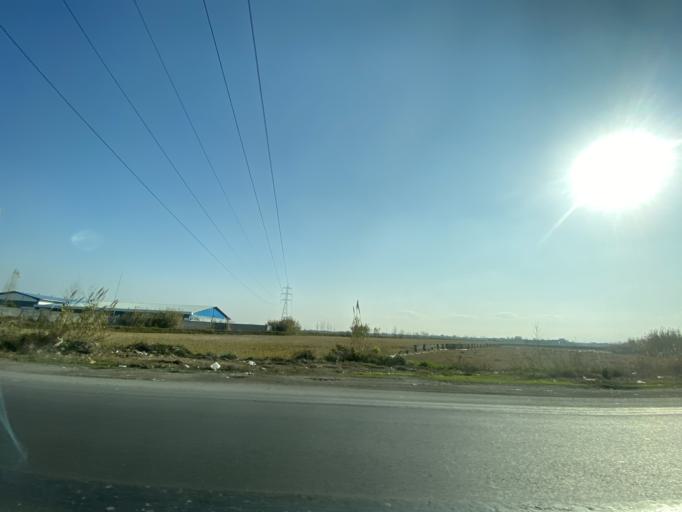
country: IR
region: Mazandaran
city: Babol
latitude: 36.5135
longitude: 52.5632
